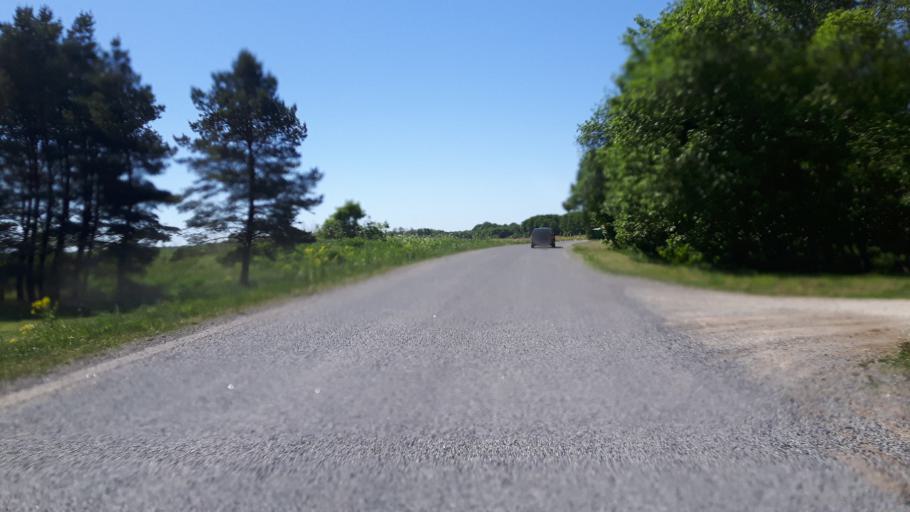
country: EE
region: Ida-Virumaa
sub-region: Sillamaee linn
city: Sillamae
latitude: 59.3744
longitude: 27.8531
